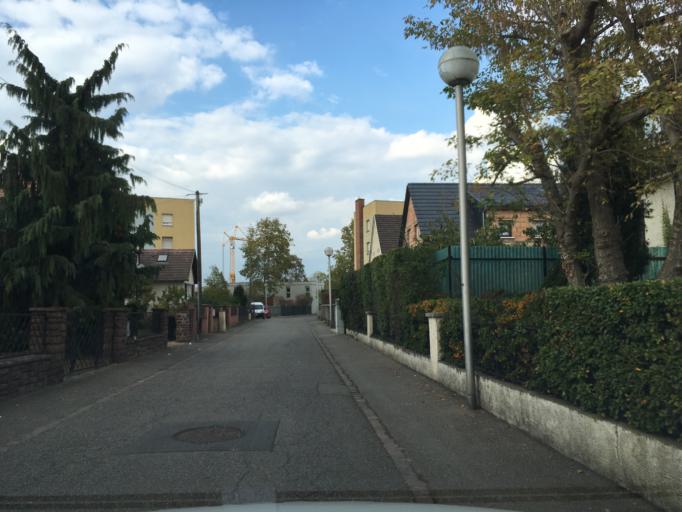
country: FR
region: Alsace
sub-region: Departement du Haut-Rhin
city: Ingersheim
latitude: 48.0881
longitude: 7.3275
